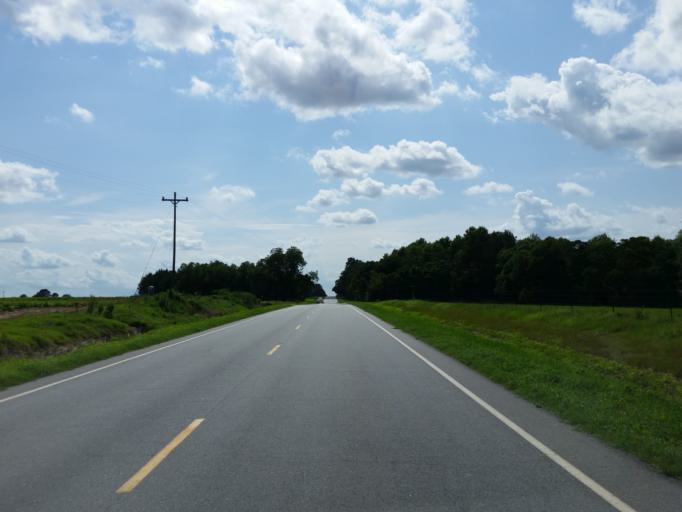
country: US
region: Georgia
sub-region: Turner County
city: Ashburn
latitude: 31.6588
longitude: -83.5708
